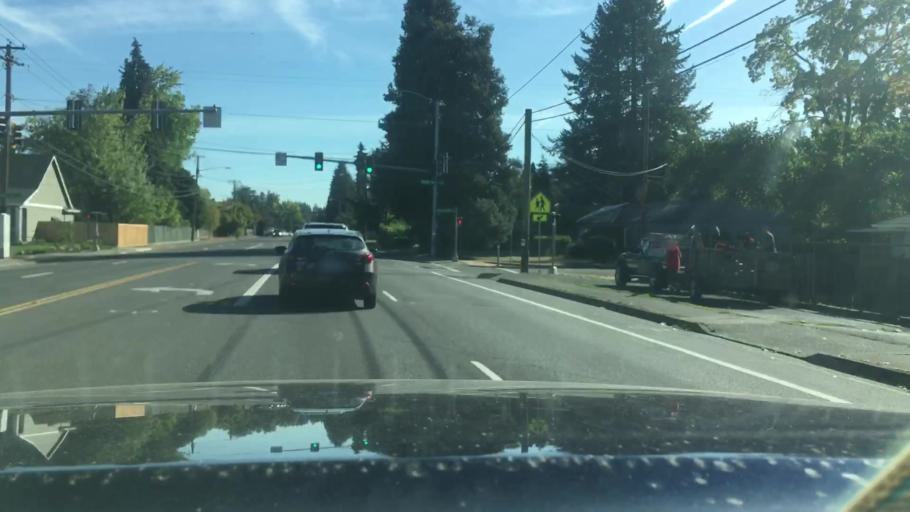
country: US
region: Oregon
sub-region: Lane County
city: Eugene
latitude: 44.0738
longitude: -123.0695
